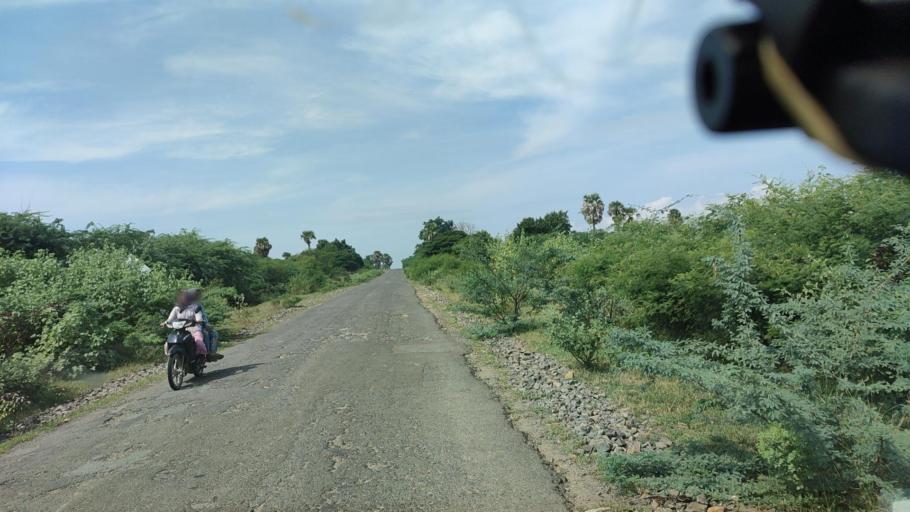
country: MM
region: Mandalay
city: Myingyan
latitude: 21.3421
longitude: 95.2852
